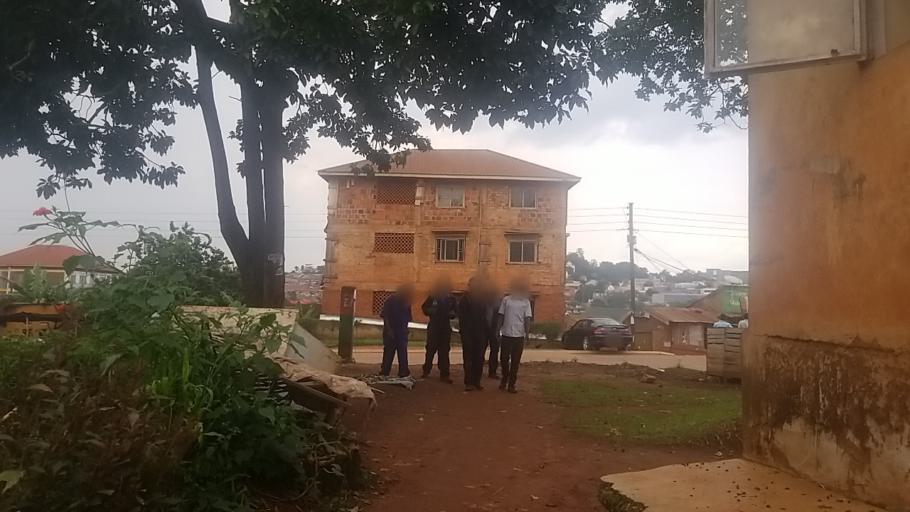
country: UG
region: Central Region
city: Kampala Central Division
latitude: 0.3391
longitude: 32.5696
